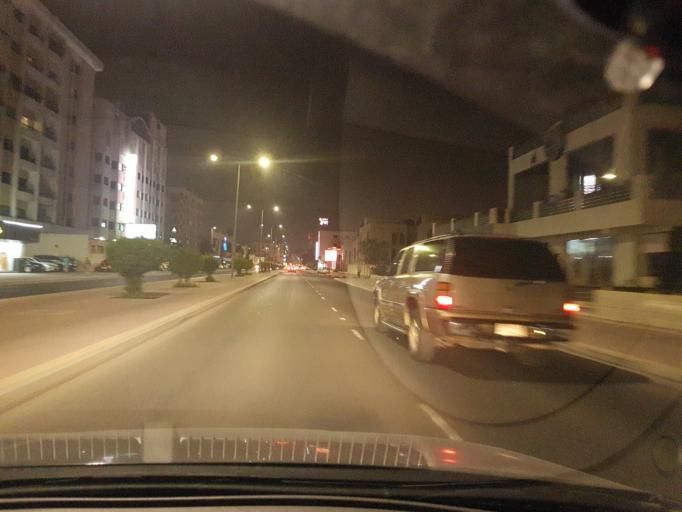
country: BH
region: Manama
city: Manama
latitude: 26.2124
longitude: 50.5916
